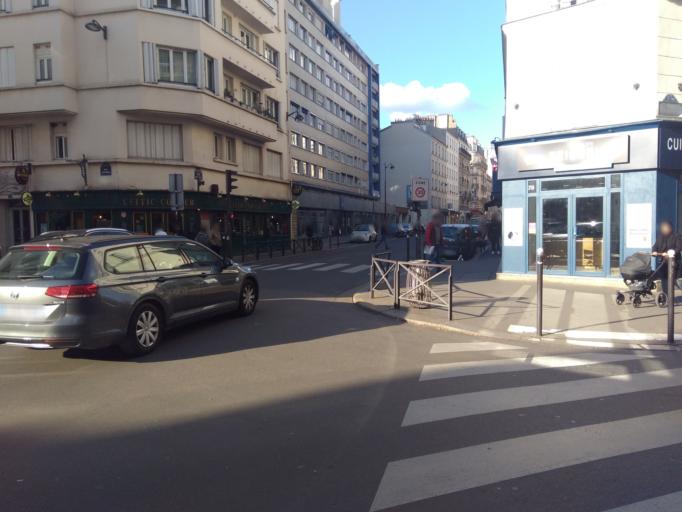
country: FR
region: Ile-de-France
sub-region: Departement des Hauts-de-Seine
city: Vanves
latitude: 48.8436
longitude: 2.2959
